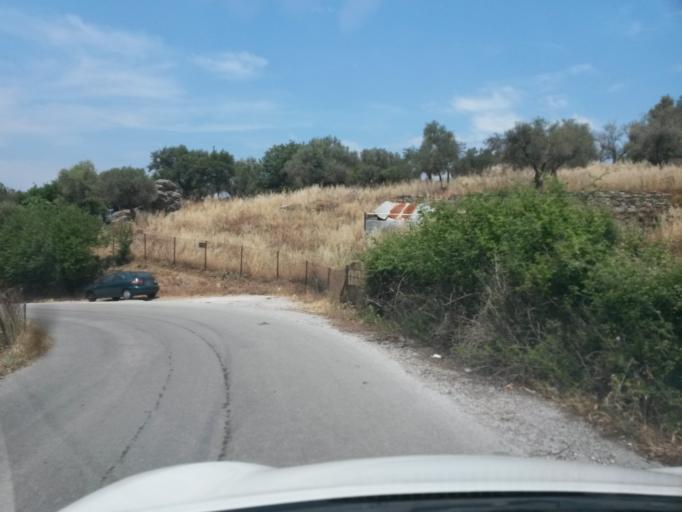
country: GR
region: North Aegean
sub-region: Nomos Lesvou
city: Pamfylla
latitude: 39.1734
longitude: 26.4836
